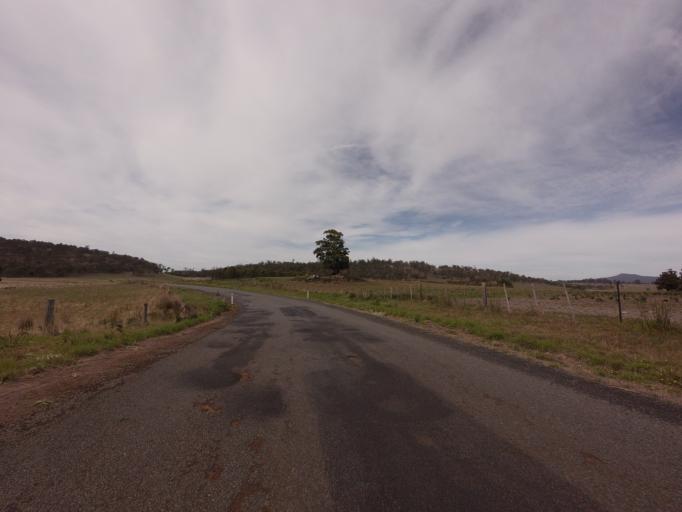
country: AU
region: Tasmania
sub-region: Sorell
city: Sorell
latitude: -42.5260
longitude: 147.6509
